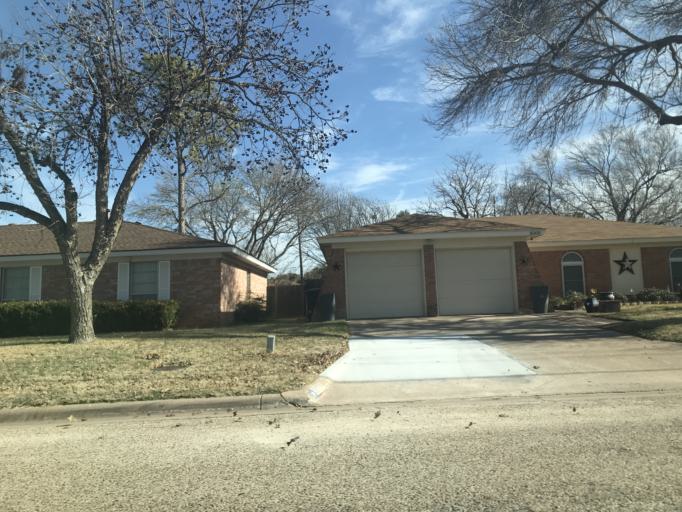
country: US
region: Texas
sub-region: Taylor County
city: Abilene
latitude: 32.4140
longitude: -99.7616
